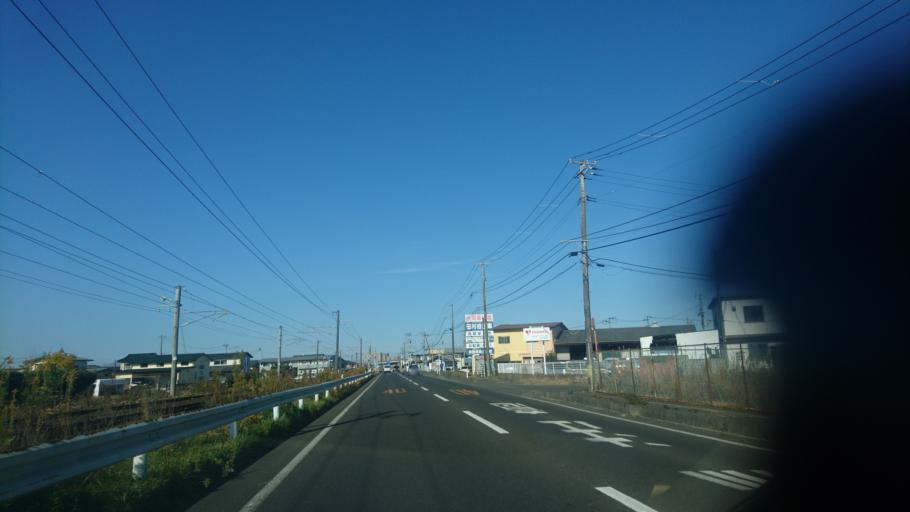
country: JP
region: Miyagi
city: Iwanuma
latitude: 38.1592
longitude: 140.8858
